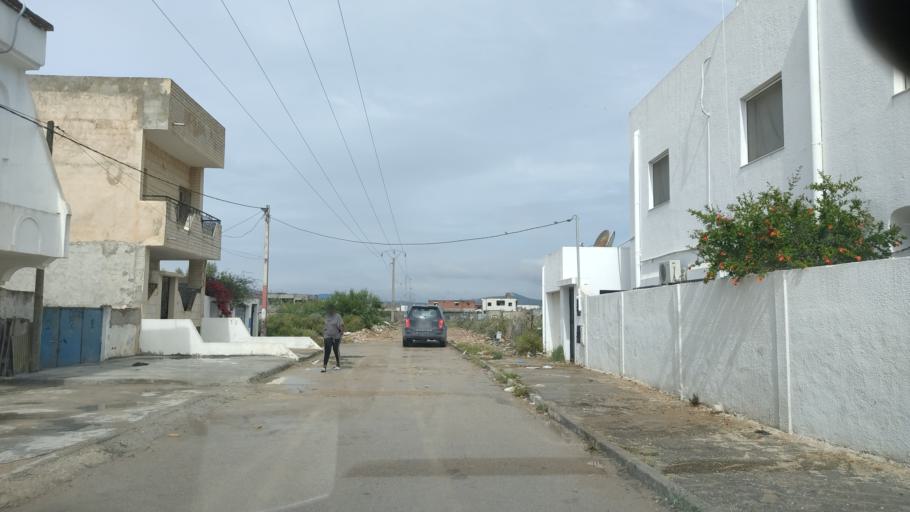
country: TN
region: Ariana
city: Ariana
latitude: 36.8874
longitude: 10.2133
